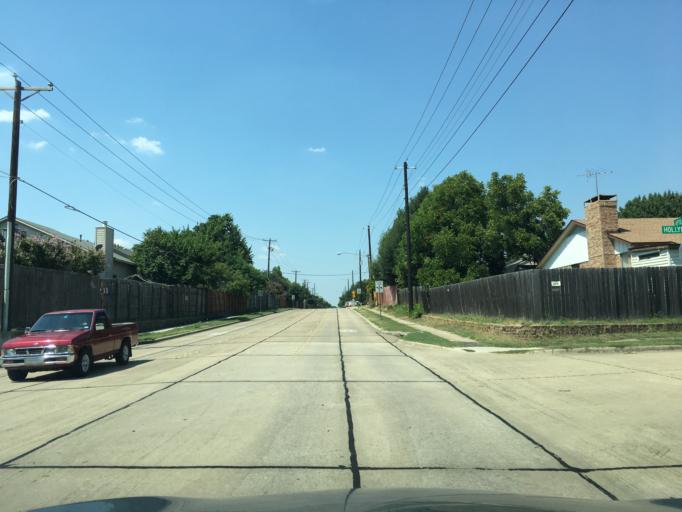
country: US
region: Texas
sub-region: Dallas County
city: Garland
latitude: 32.9515
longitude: -96.6667
